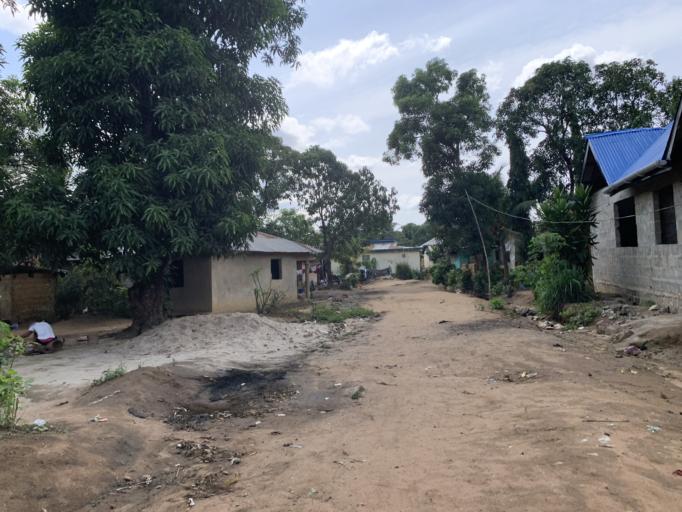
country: SL
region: Western Area
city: Waterloo
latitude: 8.3368
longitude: -13.0459
